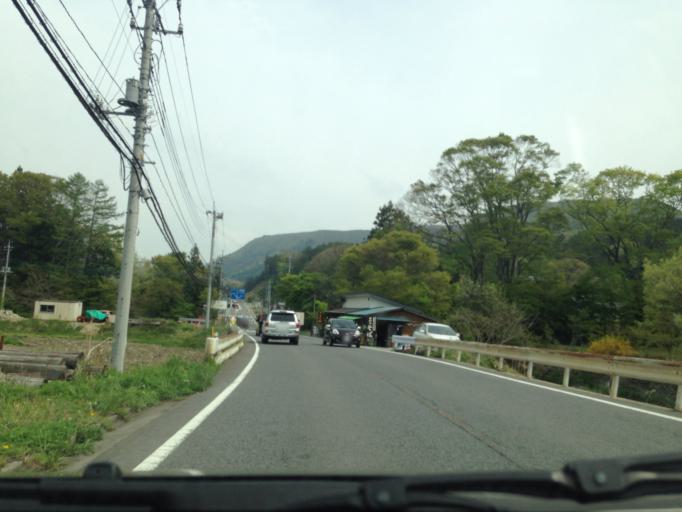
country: JP
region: Tochigi
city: Yaita
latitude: 36.9822
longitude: 139.7867
